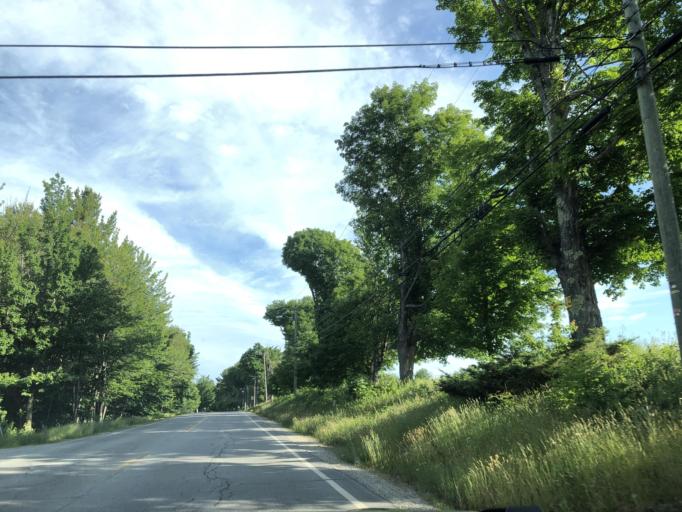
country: US
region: New Hampshire
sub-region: Merrimack County
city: New London
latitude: 43.4055
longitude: -71.9703
